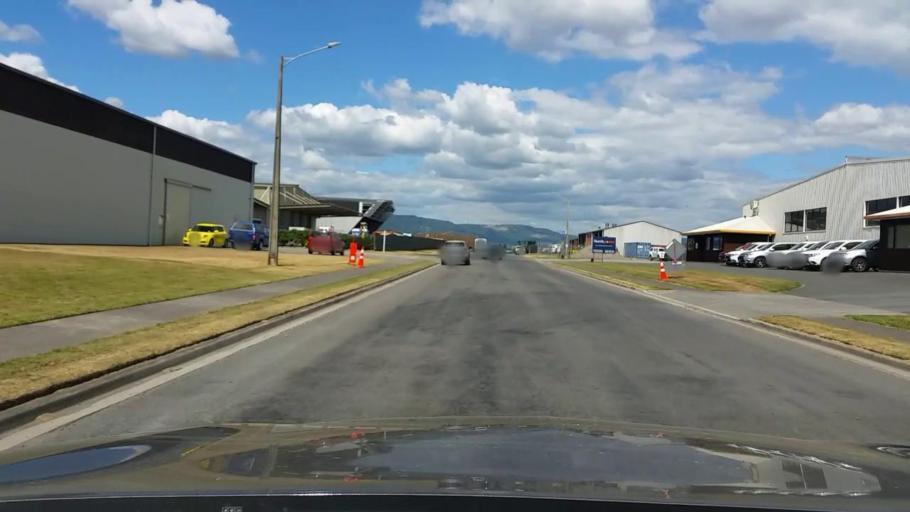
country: NZ
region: Waikato
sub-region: Matamata-Piako District
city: Matamata
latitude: -37.8158
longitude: 175.7936
